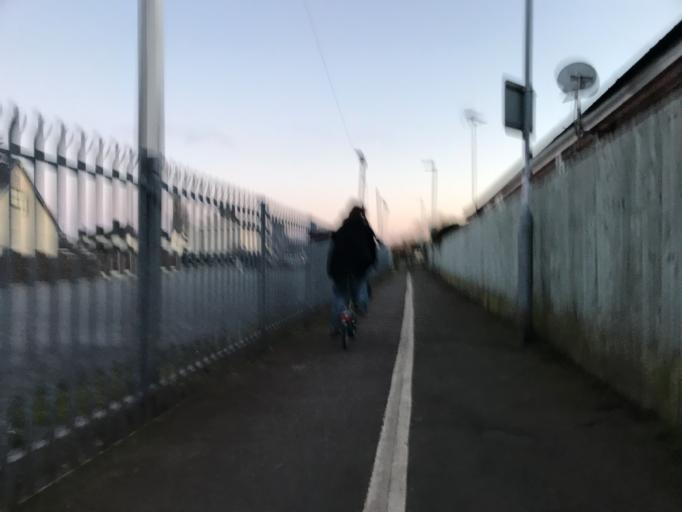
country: GB
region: England
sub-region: Lincolnshire
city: Holton le Clay
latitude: 53.5245
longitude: -0.0638
